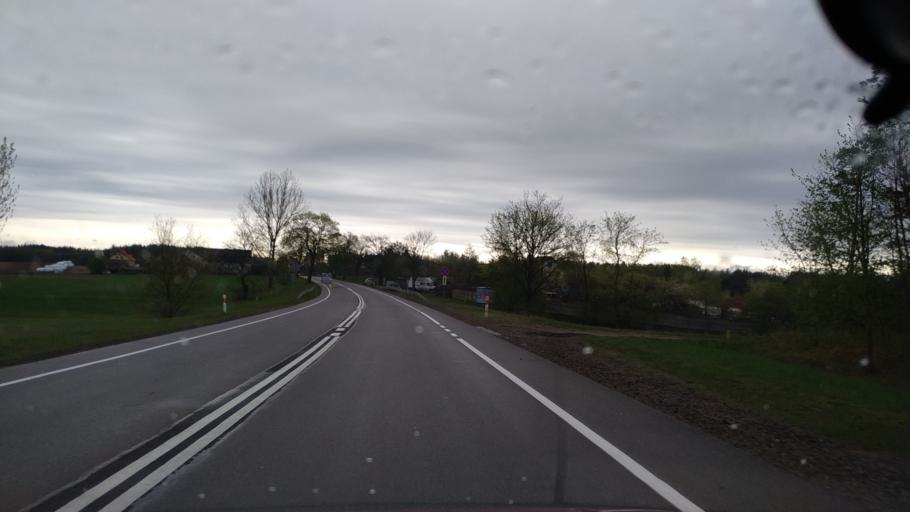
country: PL
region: Pomeranian Voivodeship
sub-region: Powiat chojnicki
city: Czersk
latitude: 53.8056
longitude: 18.0159
